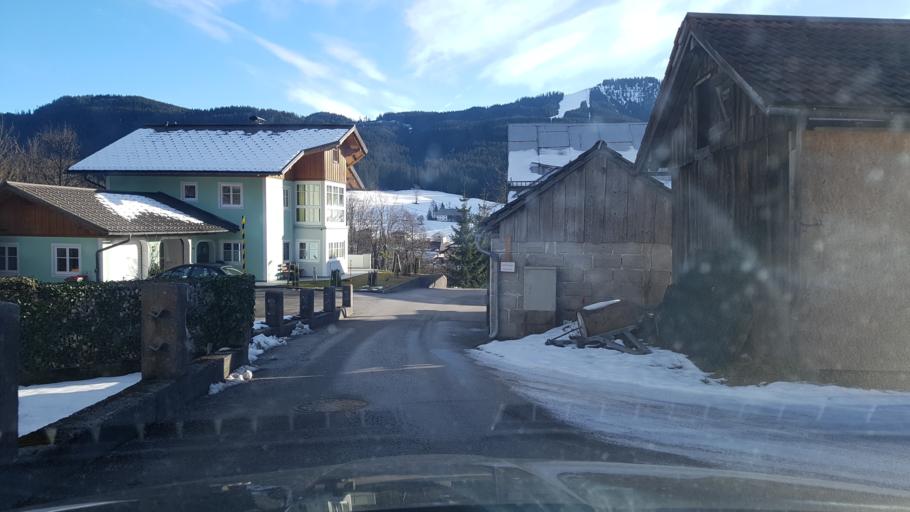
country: AT
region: Salzburg
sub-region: Politischer Bezirk Salzburg-Umgebung
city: Strobl
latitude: 47.5949
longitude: 13.4656
